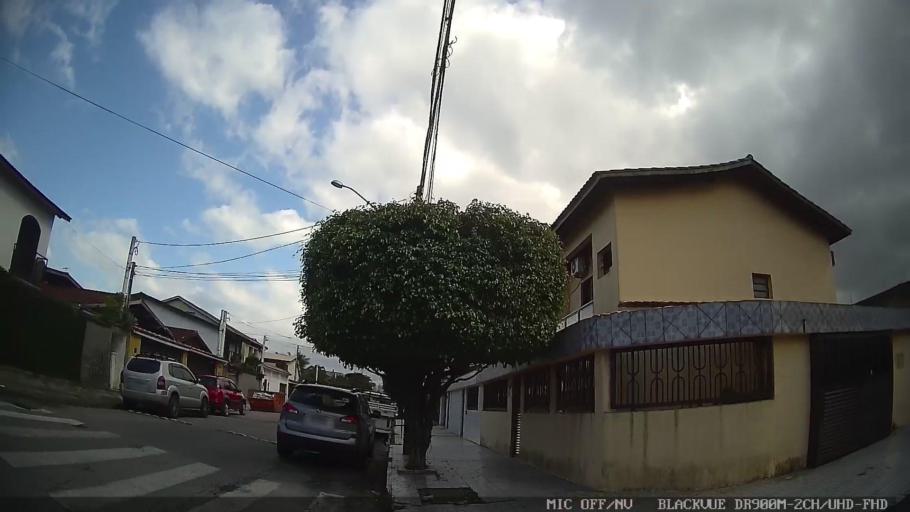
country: BR
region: Sao Paulo
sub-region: Guaruja
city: Guaruja
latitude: -23.9932
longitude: -46.2760
